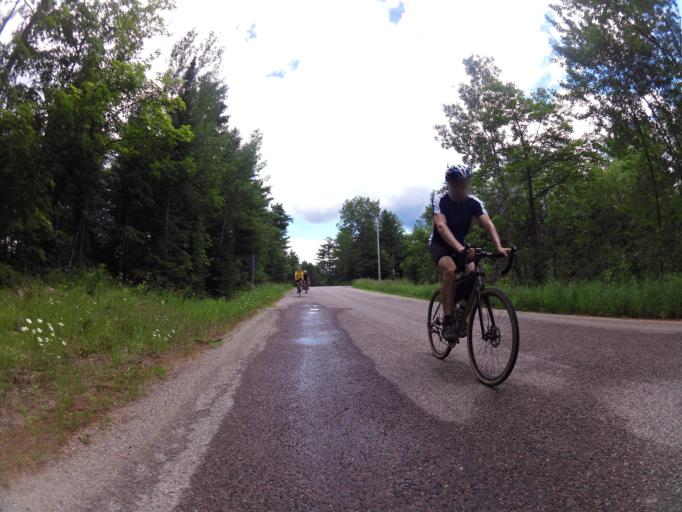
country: CA
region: Ontario
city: Renfrew
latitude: 45.0395
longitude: -76.7121
